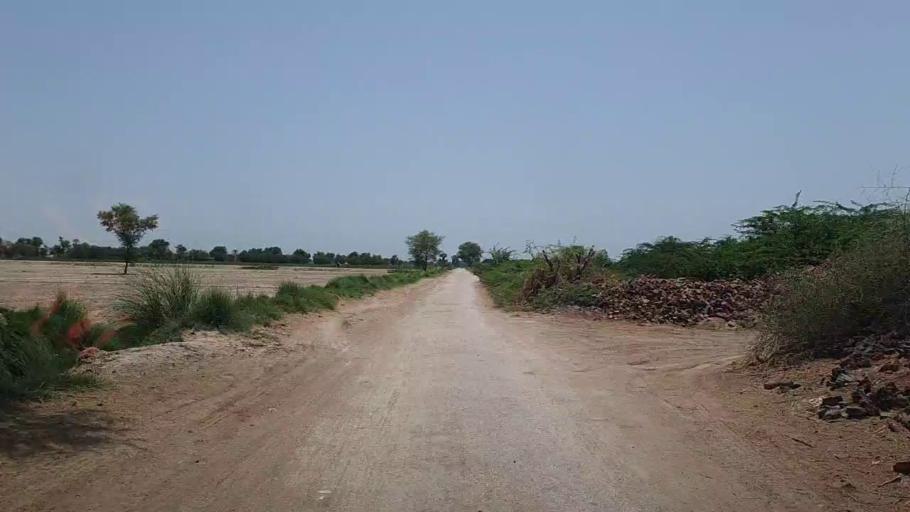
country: PK
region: Sindh
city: Pad Idan
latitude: 26.7548
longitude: 68.2936
